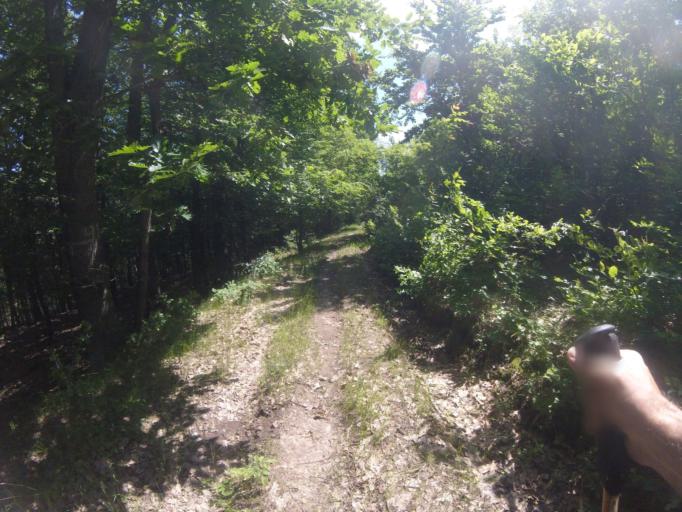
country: HU
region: Nograd
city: Matraverebely
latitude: 47.9288
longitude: 19.8046
